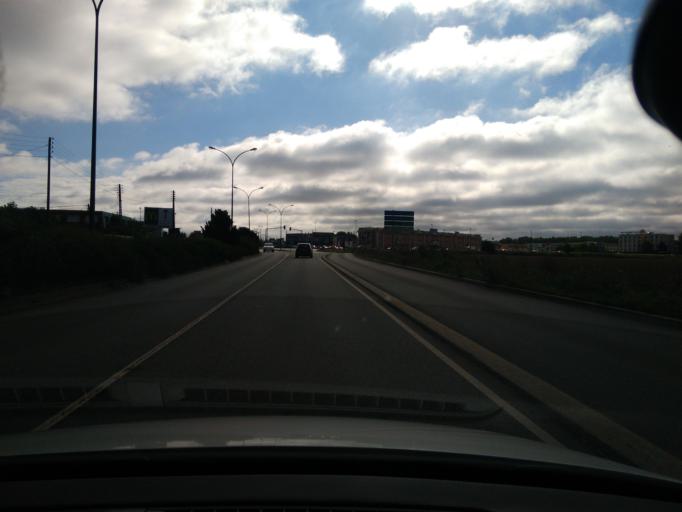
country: FR
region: Ile-de-France
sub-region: Departement de l'Essonne
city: Massy
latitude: 48.7164
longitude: 2.2963
